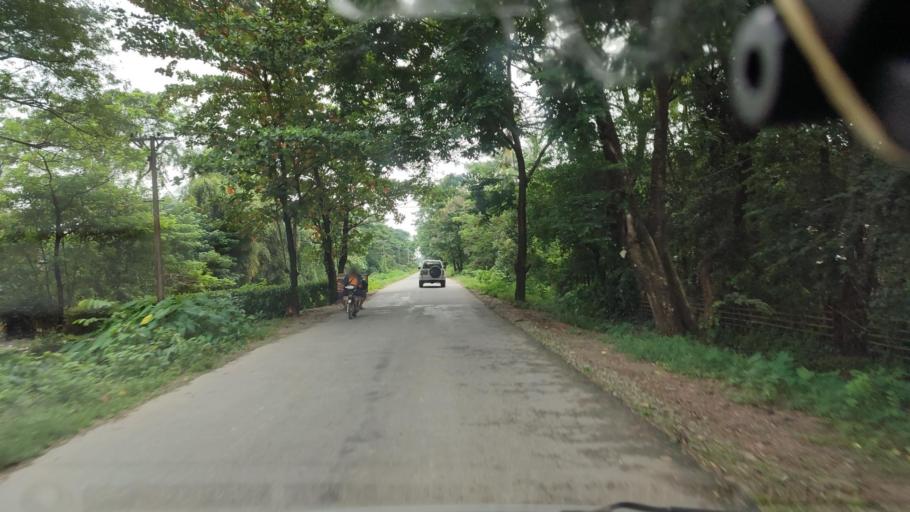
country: MM
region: Bago
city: Thanatpin
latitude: 17.1032
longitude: 96.5175
